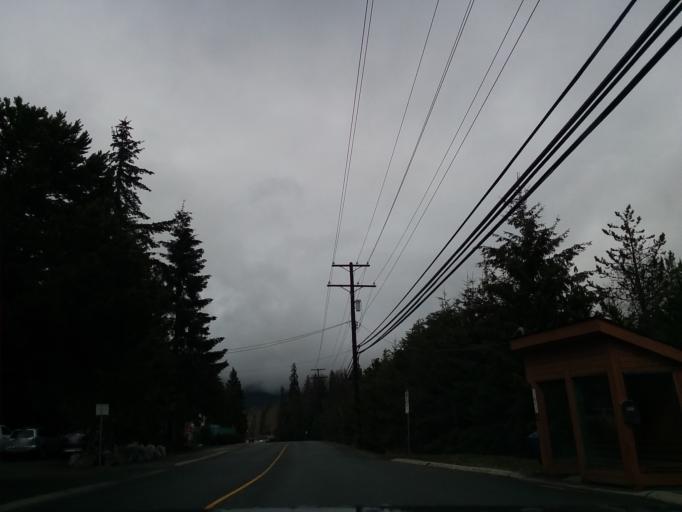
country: CA
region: British Columbia
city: Whistler
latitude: 50.1283
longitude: -122.9548
